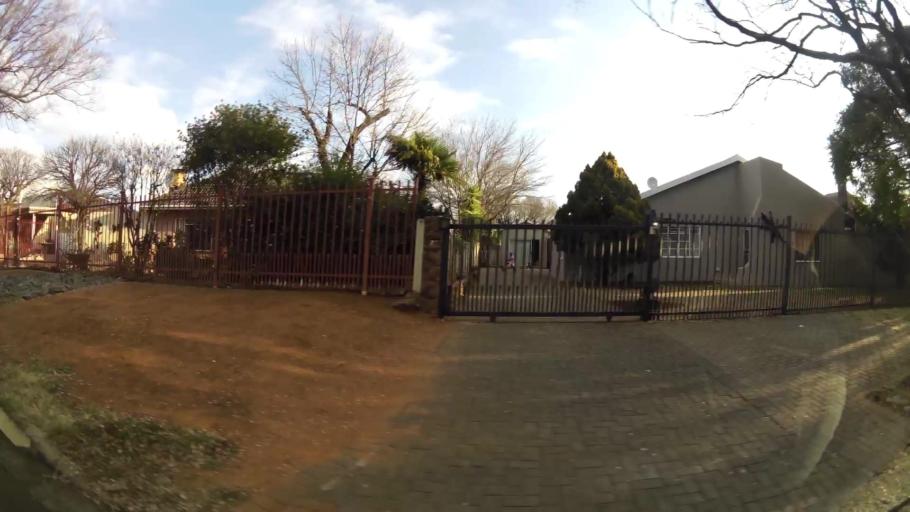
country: ZA
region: Orange Free State
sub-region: Mangaung Metropolitan Municipality
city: Bloemfontein
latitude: -29.1404
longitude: 26.1954
